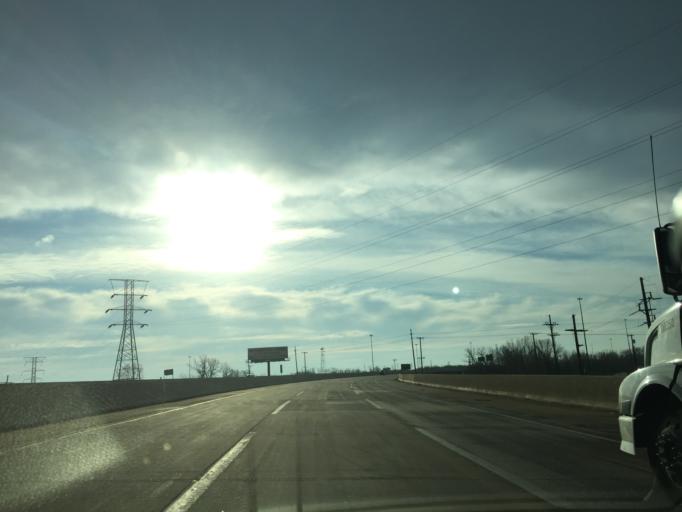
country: US
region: Indiana
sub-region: Lake County
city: Gary
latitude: 41.6001
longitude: -87.3081
